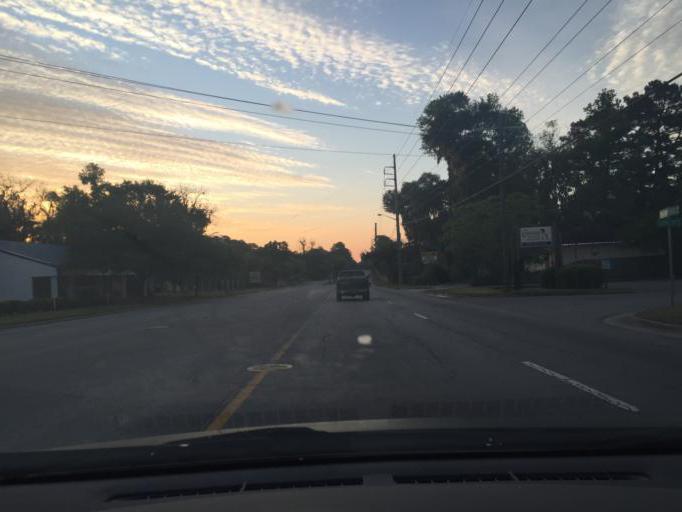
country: US
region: Georgia
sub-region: Chatham County
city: Isle of Hope
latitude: 31.9936
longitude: -81.1036
